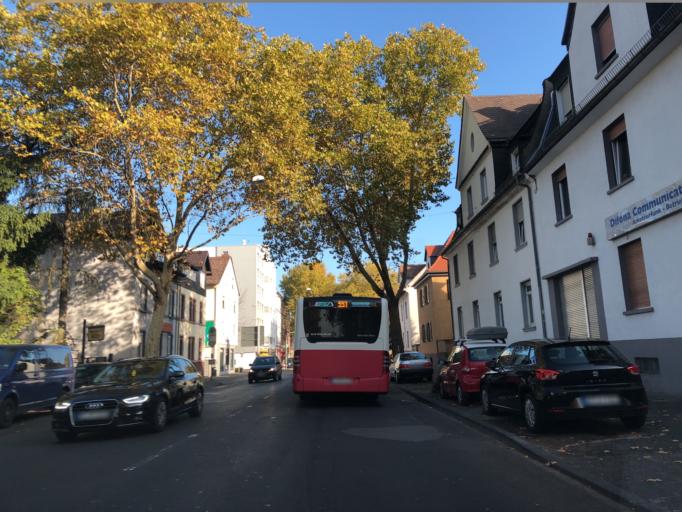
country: DE
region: Hesse
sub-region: Regierungsbezirk Darmstadt
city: Offenbach
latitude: 50.0923
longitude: 8.7517
